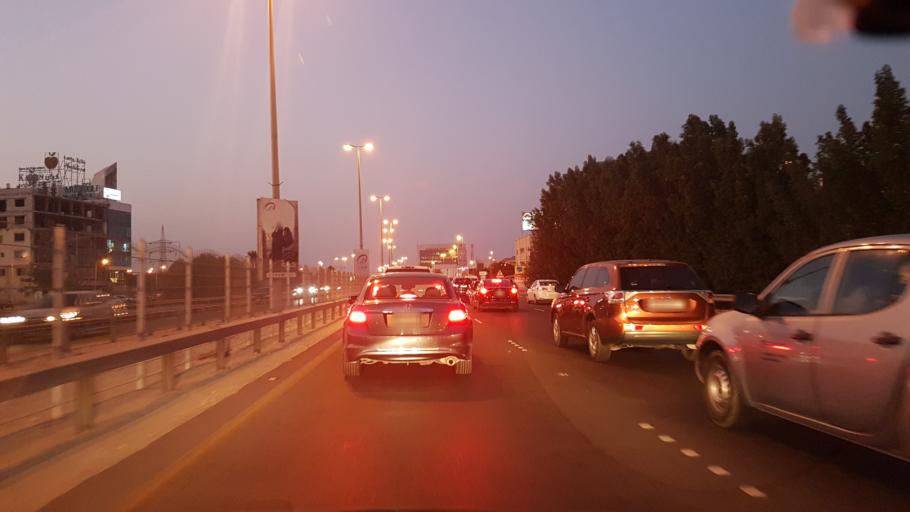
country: BH
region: Northern
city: Madinat `Isa
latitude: 26.1833
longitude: 50.5373
